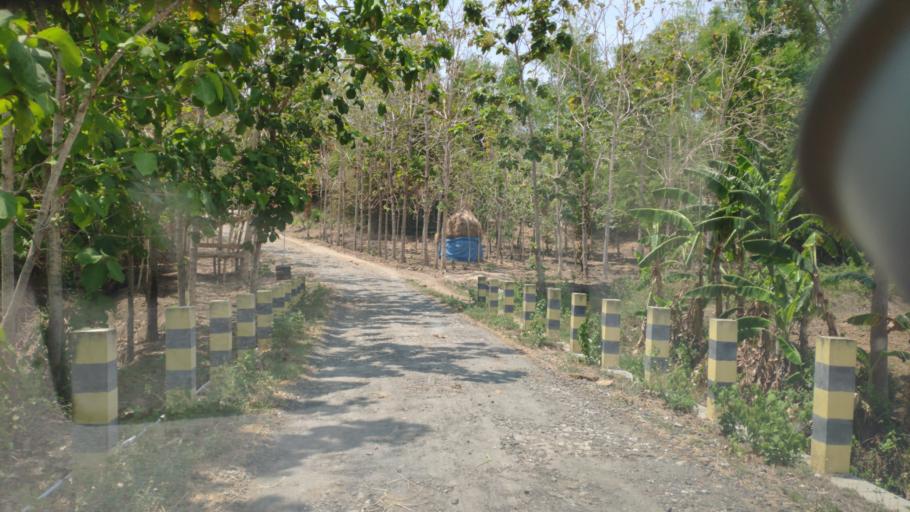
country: ID
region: Central Java
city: Karangtengah
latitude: -7.0415
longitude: 111.3185
